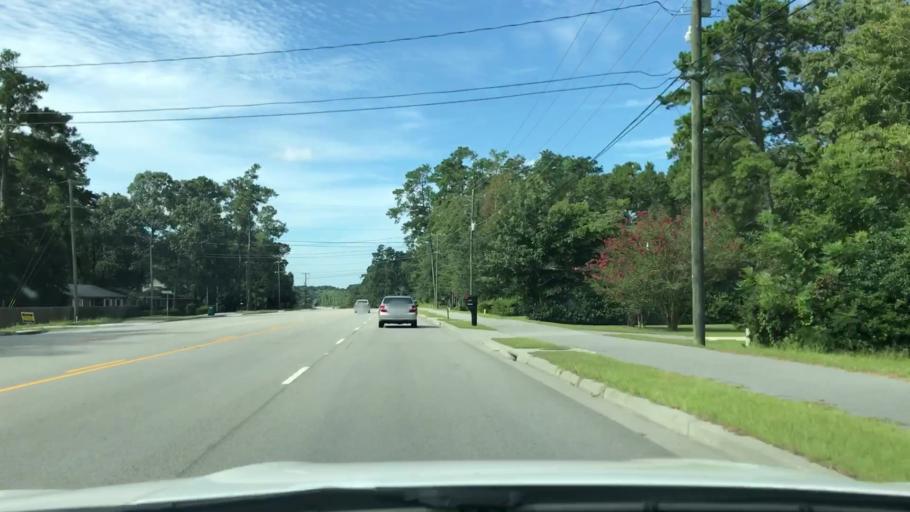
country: US
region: South Carolina
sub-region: Dorchester County
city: Centerville
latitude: 32.9856
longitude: -80.1930
